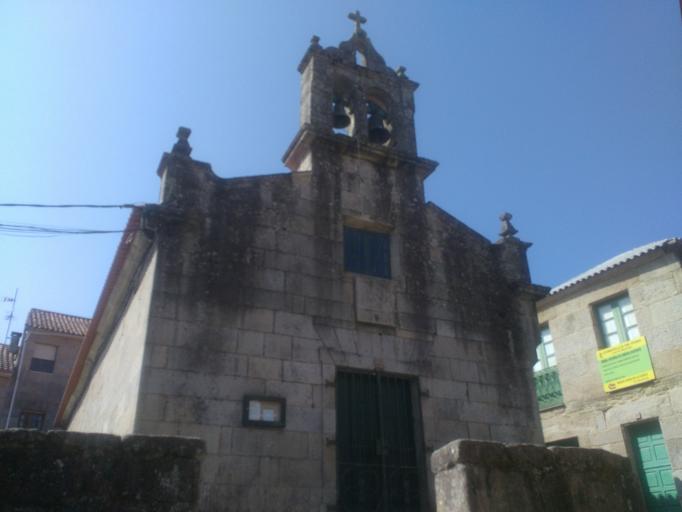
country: ES
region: Galicia
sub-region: Provincia de Pontevedra
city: Combarro
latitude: 42.4321
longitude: -8.7049
